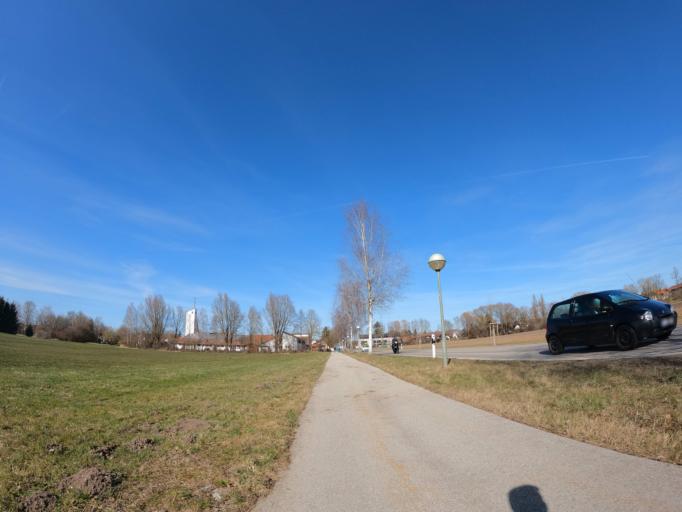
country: DE
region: Bavaria
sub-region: Upper Bavaria
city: Taufkirchen
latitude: 48.0403
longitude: 11.6174
